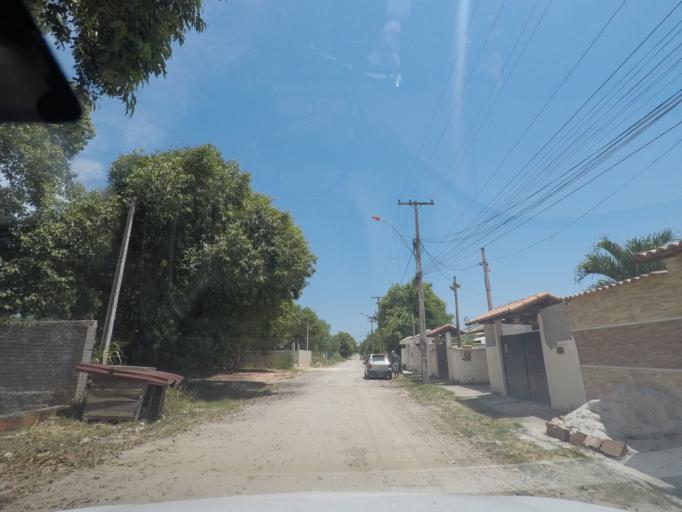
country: BR
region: Rio de Janeiro
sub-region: Niteroi
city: Niteroi
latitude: -22.9574
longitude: -42.9694
